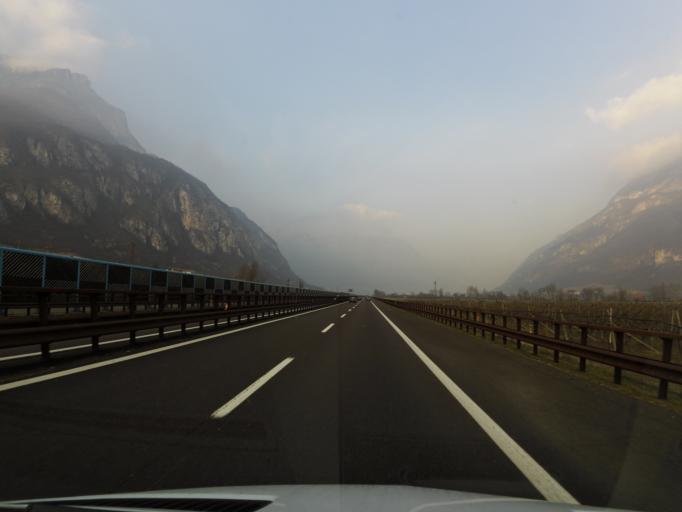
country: IT
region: Trentino-Alto Adige
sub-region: Provincia di Trento
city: Avio
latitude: 45.7032
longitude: 10.9234
